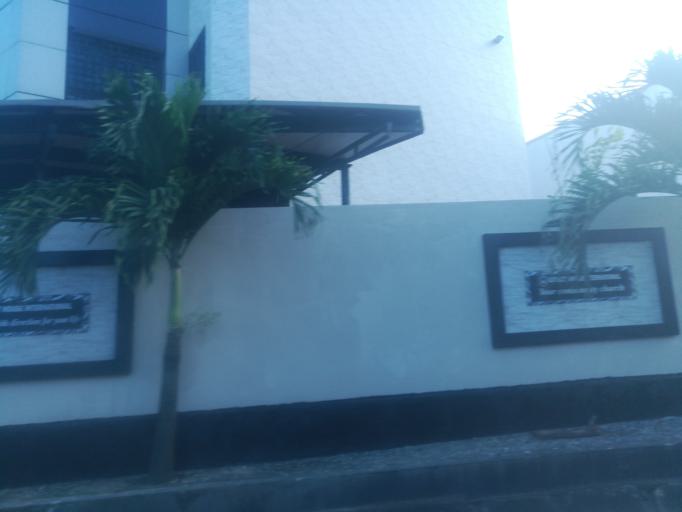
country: NG
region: Lagos
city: Agege
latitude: 6.6267
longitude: 3.3547
